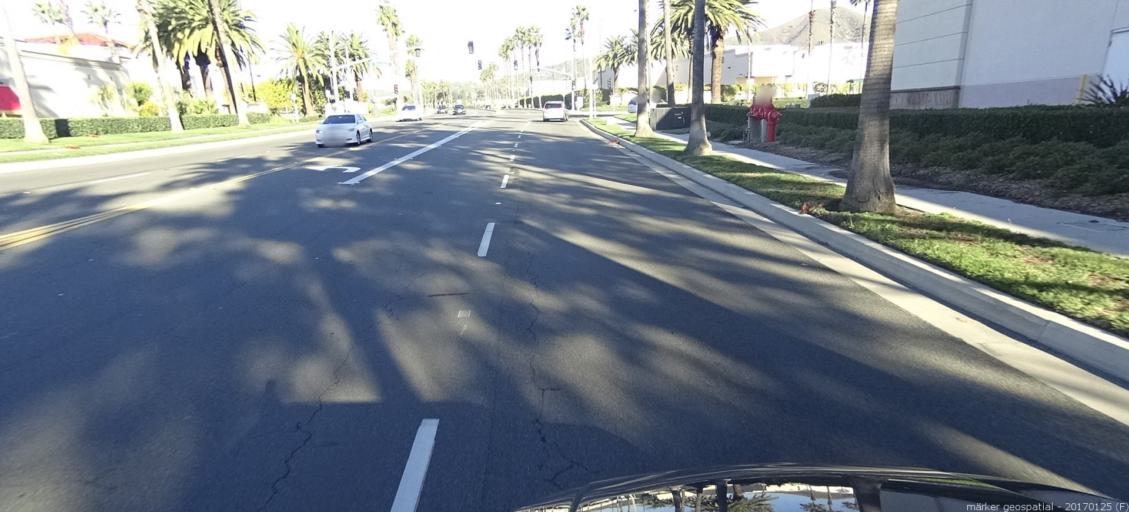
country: US
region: California
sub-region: Orange County
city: Foothill Ranch
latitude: 33.6787
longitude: -117.6666
